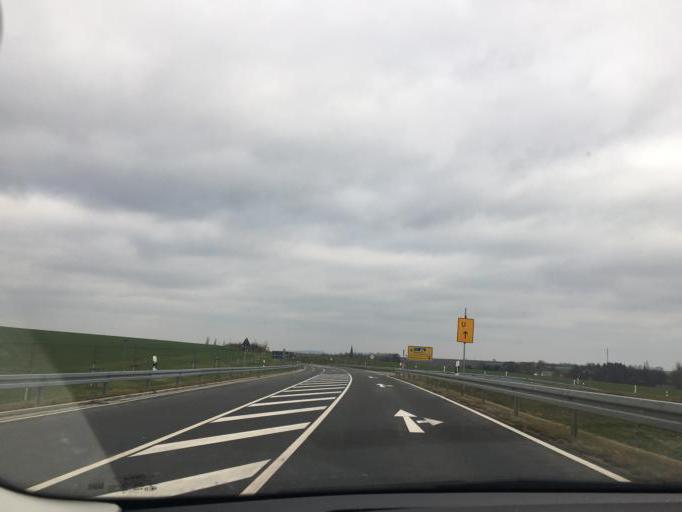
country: DE
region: Saxony
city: Niederfrohna
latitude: 50.8910
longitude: 12.7162
